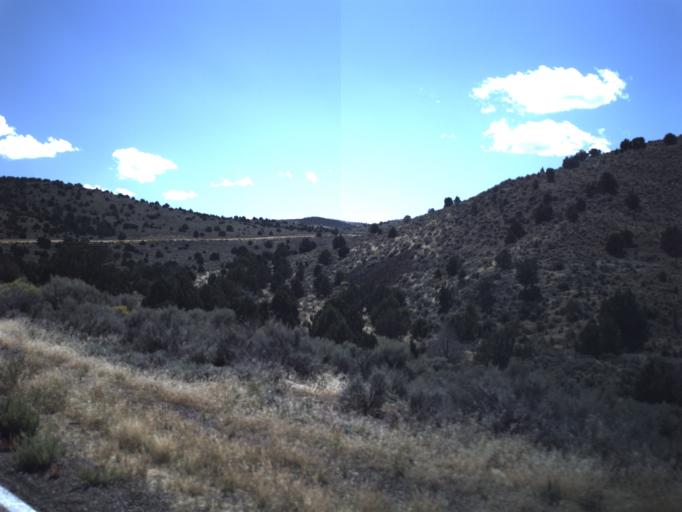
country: US
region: Utah
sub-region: Beaver County
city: Milford
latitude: 38.1245
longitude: -112.9542
